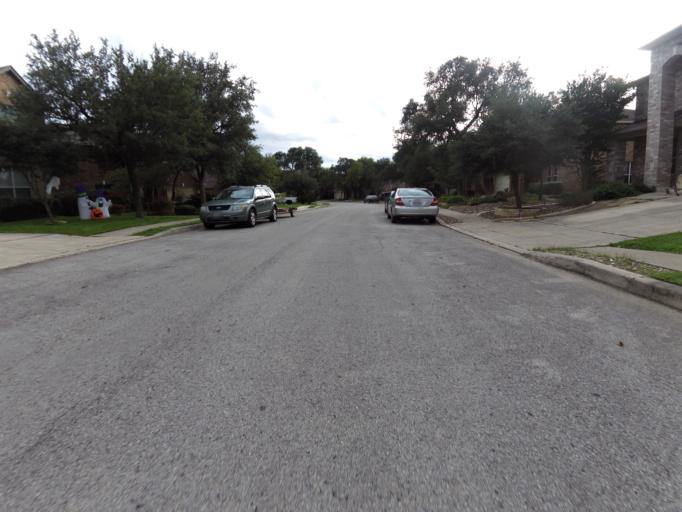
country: US
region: Texas
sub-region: Bexar County
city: Cross Mountain
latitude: 29.6715
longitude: -98.6405
